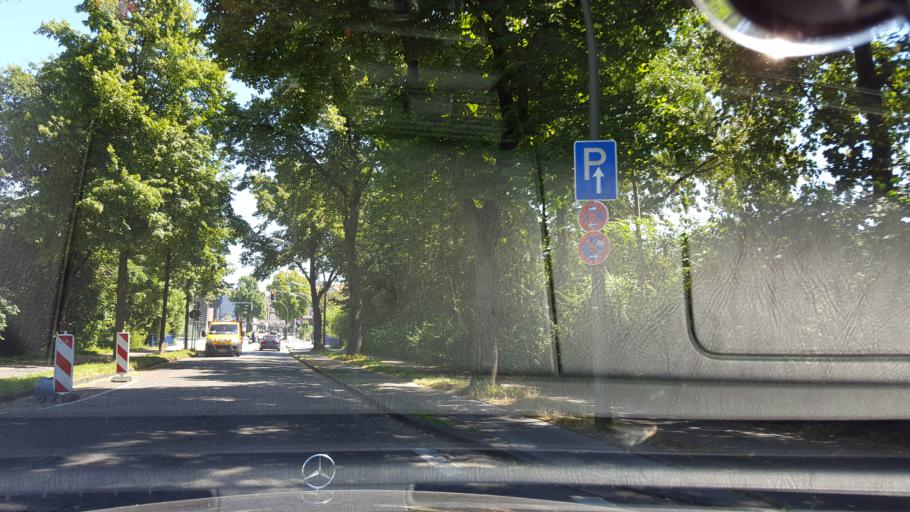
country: DE
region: North Rhine-Westphalia
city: Marl
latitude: 51.6626
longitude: 7.1271
